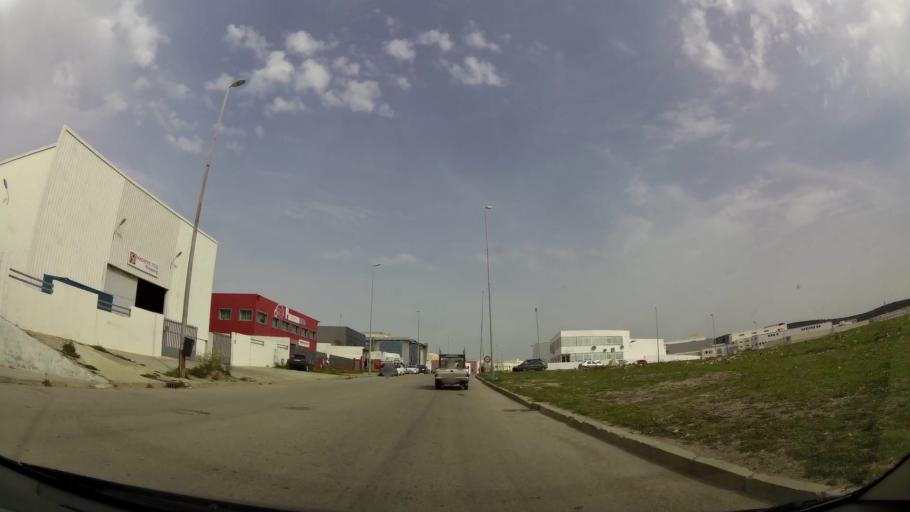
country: MA
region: Tanger-Tetouan
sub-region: Tanger-Assilah
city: Boukhalef
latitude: 35.7154
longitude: -5.8990
